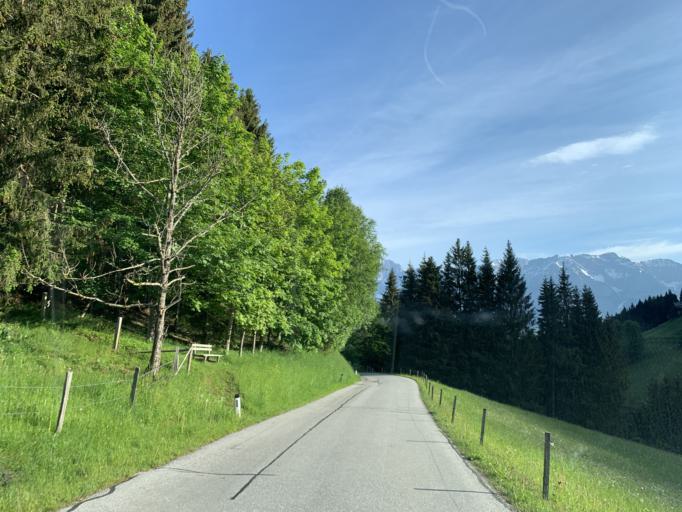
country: AT
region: Styria
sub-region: Politischer Bezirk Liezen
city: Schladming
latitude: 47.3684
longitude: 13.6151
